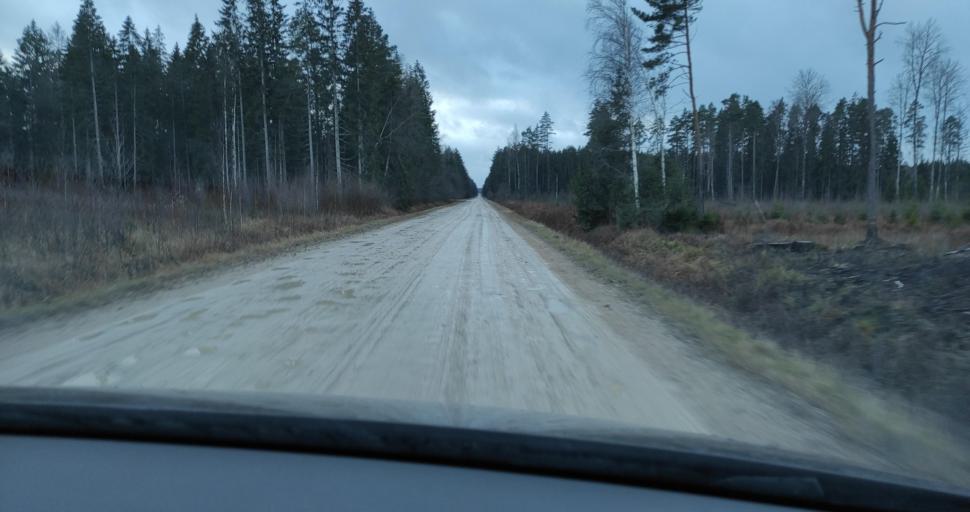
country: LV
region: Skrunda
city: Skrunda
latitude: 56.7390
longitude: 22.2050
